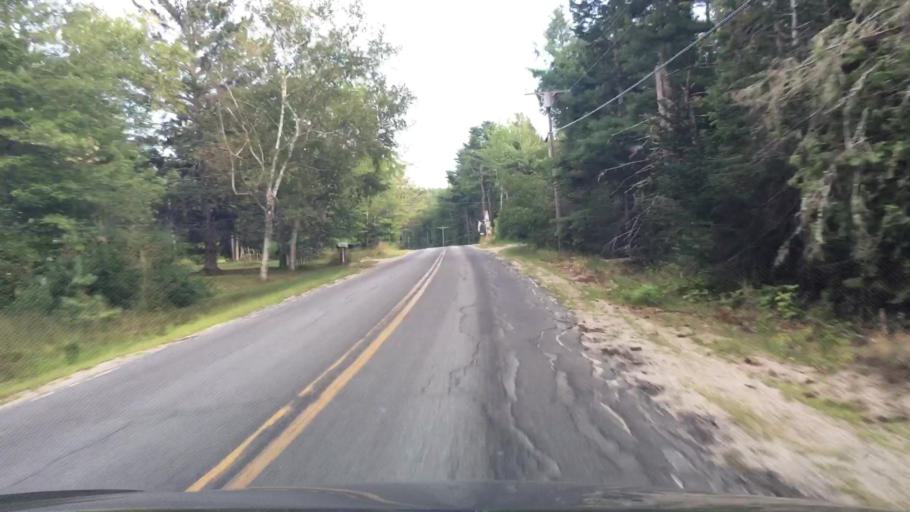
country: US
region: Maine
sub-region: Hancock County
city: Surry
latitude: 44.5070
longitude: -68.5952
